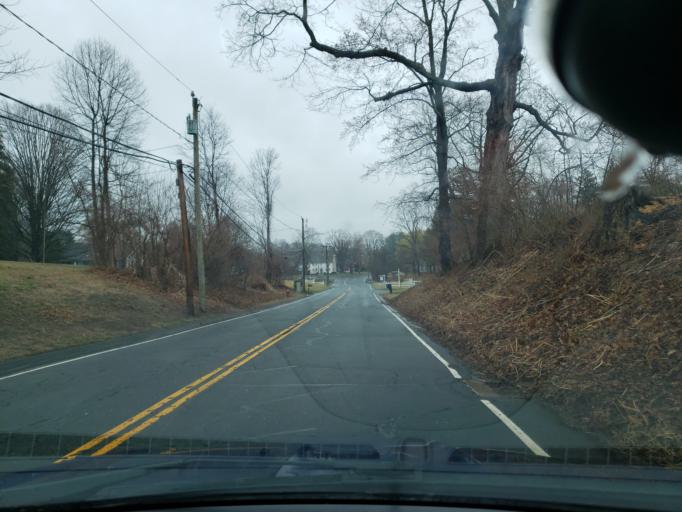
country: US
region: Connecticut
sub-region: Hartford County
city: Windsor
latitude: 41.8888
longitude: -72.6759
